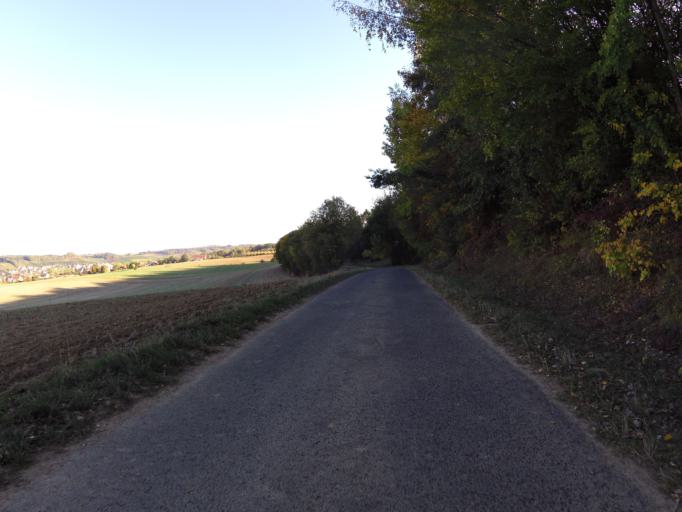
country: DE
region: Bavaria
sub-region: Regierungsbezirk Unterfranken
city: Eibelstadt
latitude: 49.7110
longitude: 9.9997
